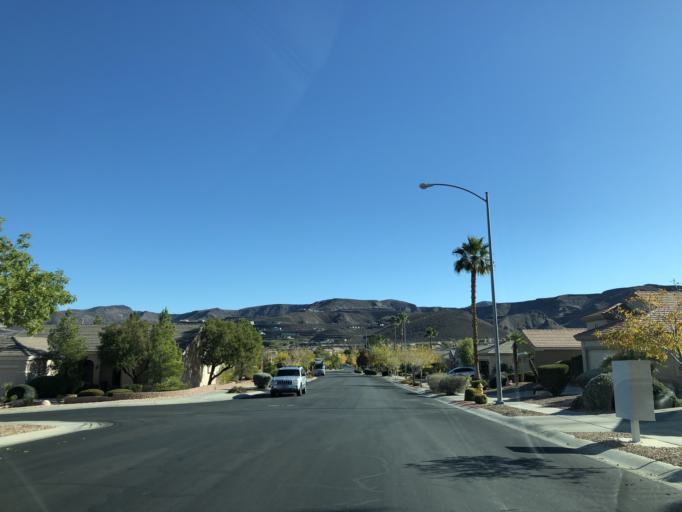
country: US
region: Nevada
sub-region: Clark County
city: Whitney
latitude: 36.0025
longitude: -115.0769
